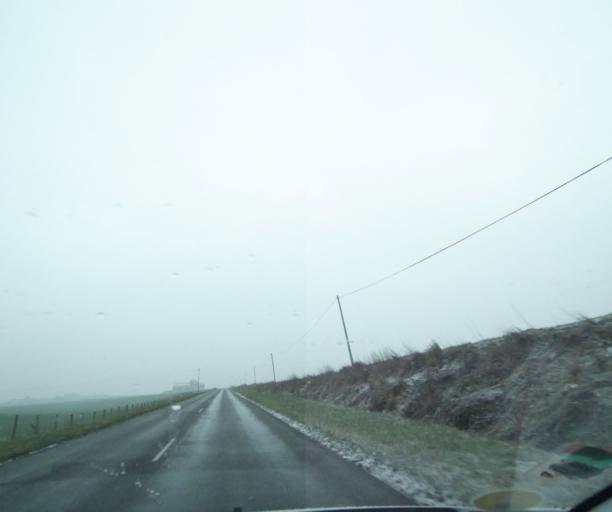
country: FR
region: Champagne-Ardenne
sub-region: Departement de la Haute-Marne
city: Wassy
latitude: 48.4878
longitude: 4.9767
